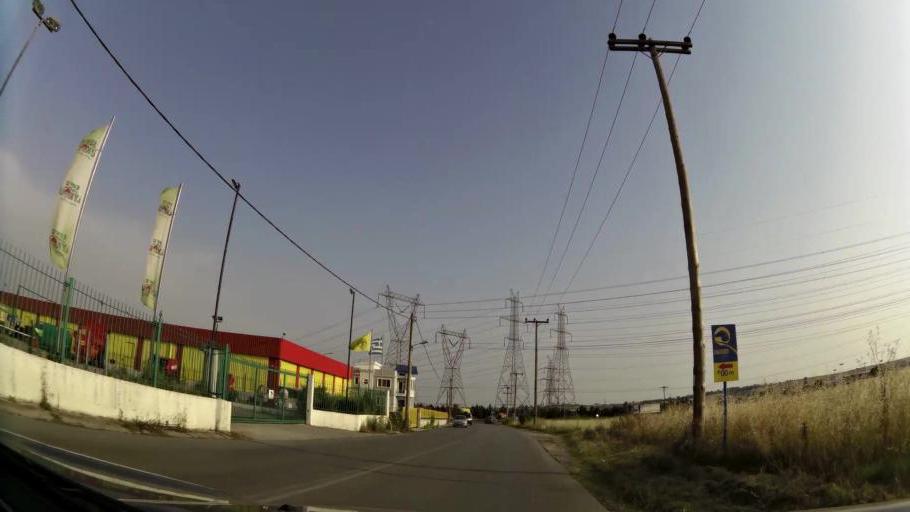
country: GR
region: Central Macedonia
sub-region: Nomos Thessalonikis
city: Oraiokastro
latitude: 40.7031
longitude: 22.9130
